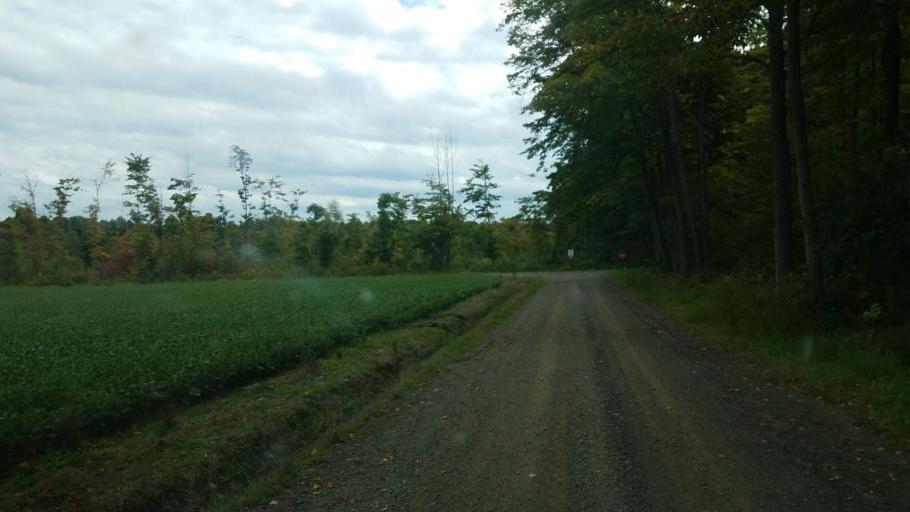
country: US
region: Pennsylvania
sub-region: Crawford County
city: Pymatuning Central
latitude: 41.5262
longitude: -80.3977
